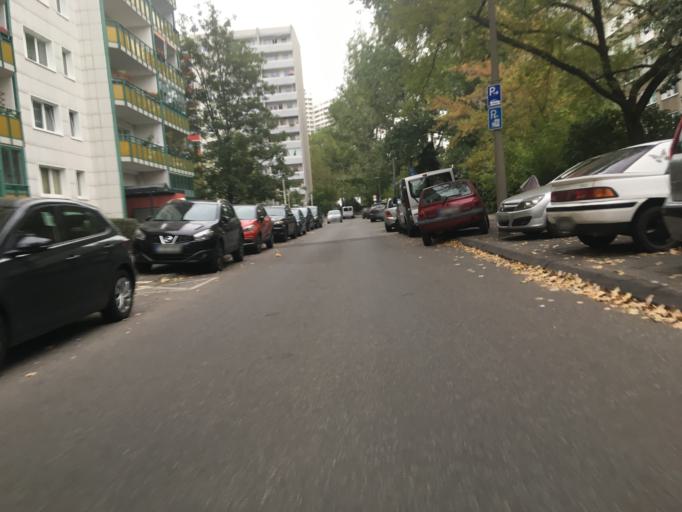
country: DE
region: Berlin
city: Fennpfuhl
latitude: 52.5263
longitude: 13.4713
